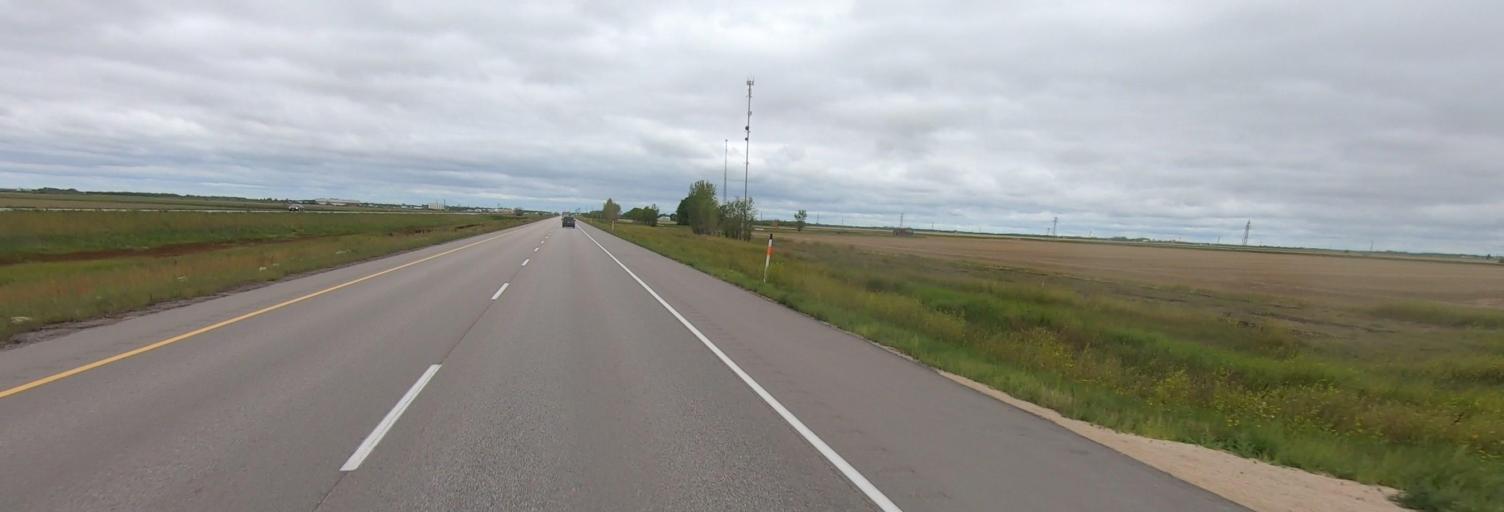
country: CA
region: Manitoba
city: Headingley
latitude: 49.8972
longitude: -97.7057
